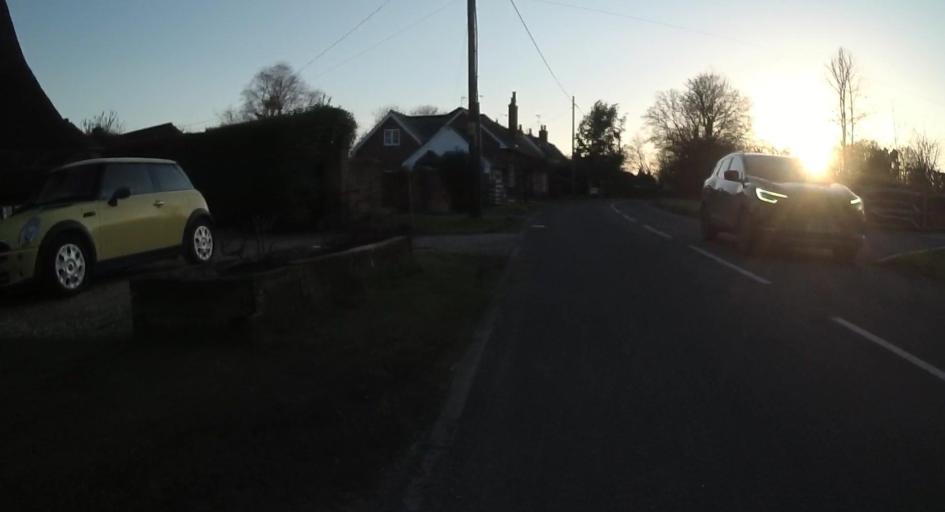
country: GB
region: England
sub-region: Hampshire
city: Fleet
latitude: 51.2691
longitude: -0.8760
